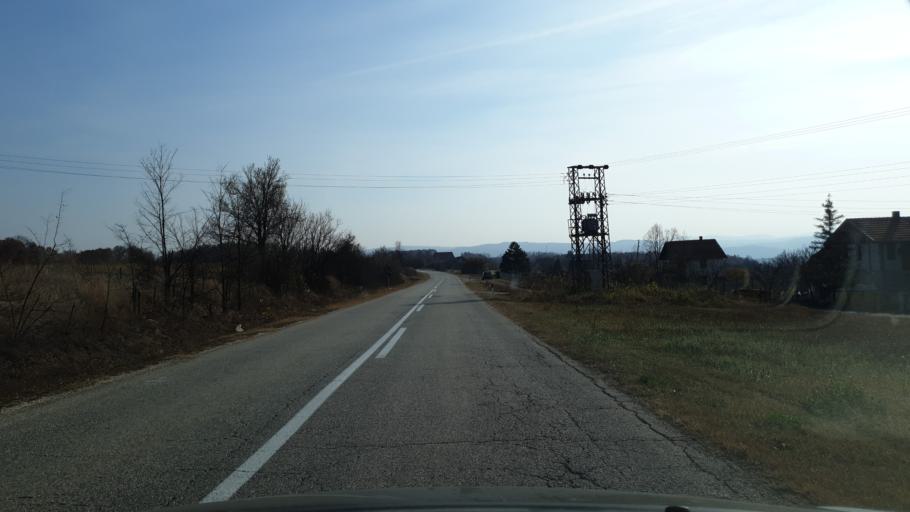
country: RS
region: Central Serbia
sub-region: Borski Okrug
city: Bor
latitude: 43.9625
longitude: 22.0863
